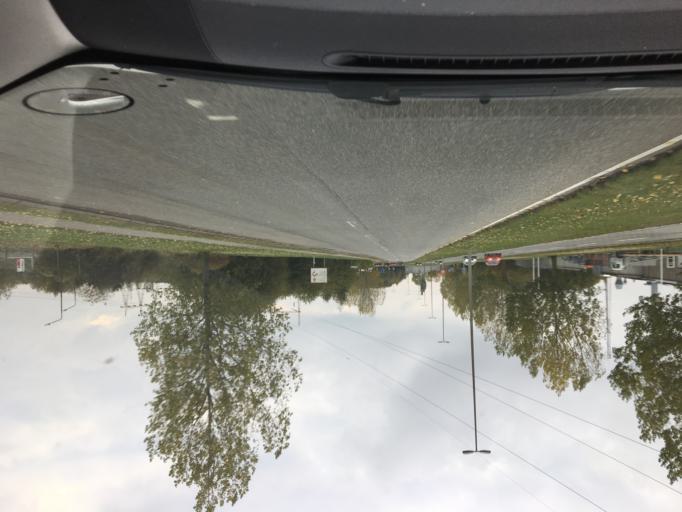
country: DK
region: South Denmark
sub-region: Fredericia Kommune
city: Fredericia
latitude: 55.5910
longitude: 9.7547
